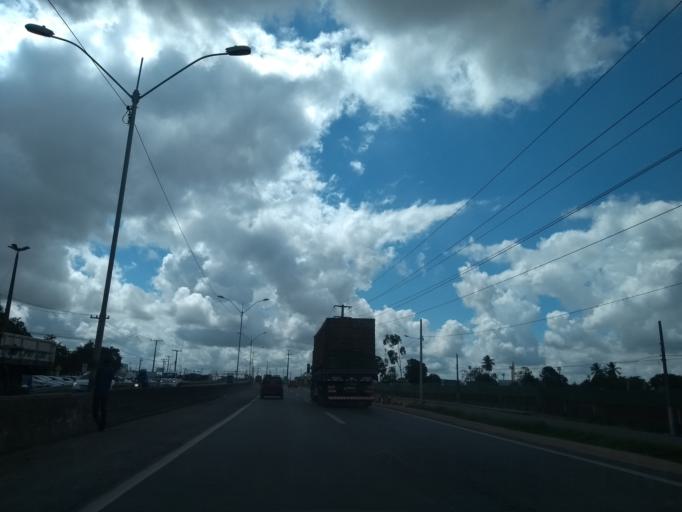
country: BR
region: Bahia
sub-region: Feira De Santana
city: Feira de Santana
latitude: -12.2780
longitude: -38.9402
